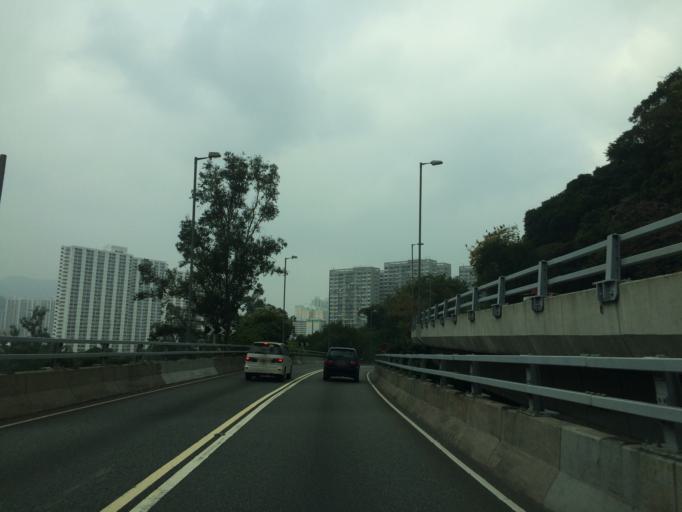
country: HK
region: Sha Tin
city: Sha Tin
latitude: 22.3719
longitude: 114.1896
